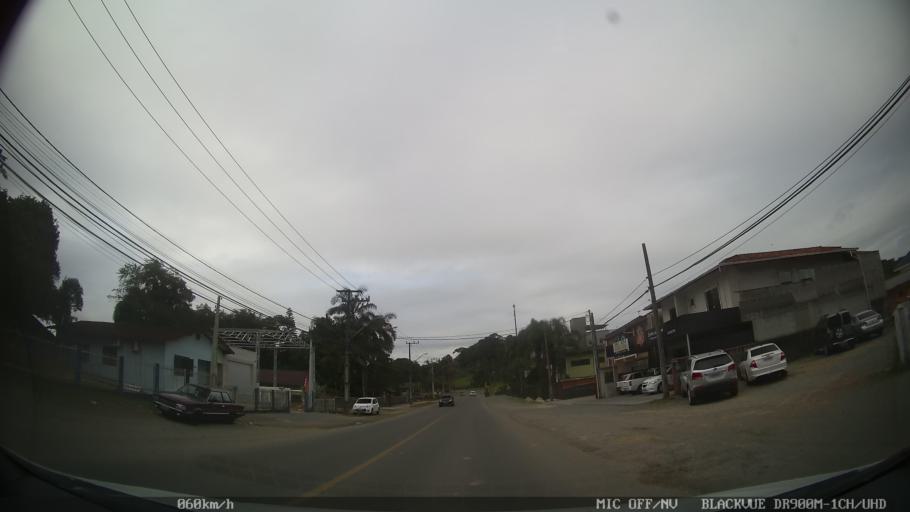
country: BR
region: Santa Catarina
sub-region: Joinville
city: Joinville
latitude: -26.3383
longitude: -48.8811
